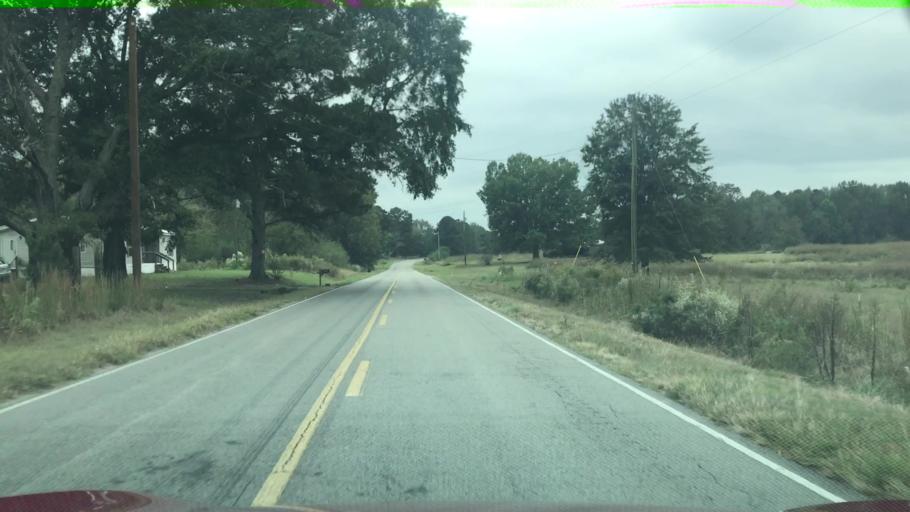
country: US
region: Alabama
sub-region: Cullman County
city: Good Hope
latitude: 34.1066
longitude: -87.0362
